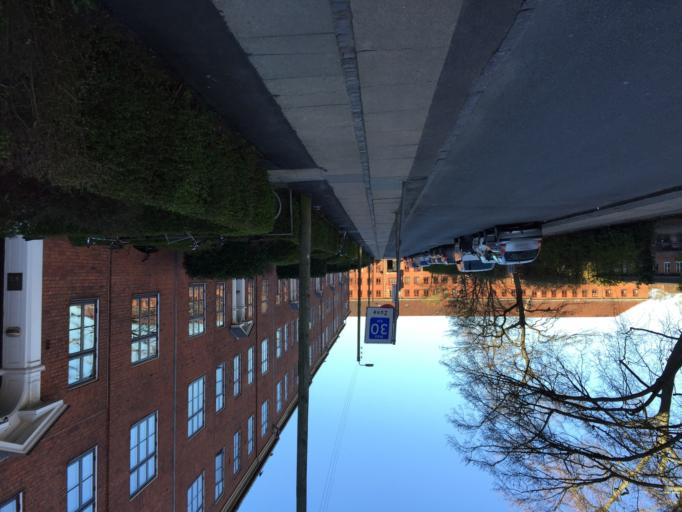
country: DK
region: Capital Region
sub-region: Frederiksberg Kommune
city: Frederiksberg
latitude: 55.6984
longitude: 12.5252
